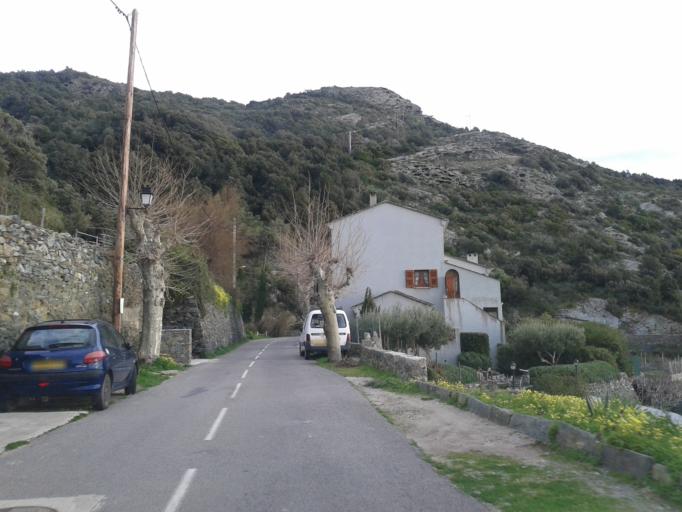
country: FR
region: Corsica
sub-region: Departement de la Haute-Corse
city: Brando
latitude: 42.8874
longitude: 9.3347
